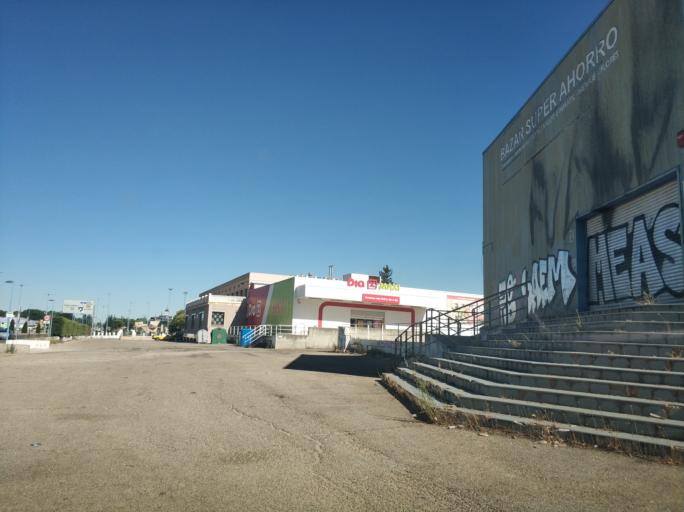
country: ES
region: Castille and Leon
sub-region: Provincia de Salamanca
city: Salamanca
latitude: 40.9518
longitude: -5.6554
